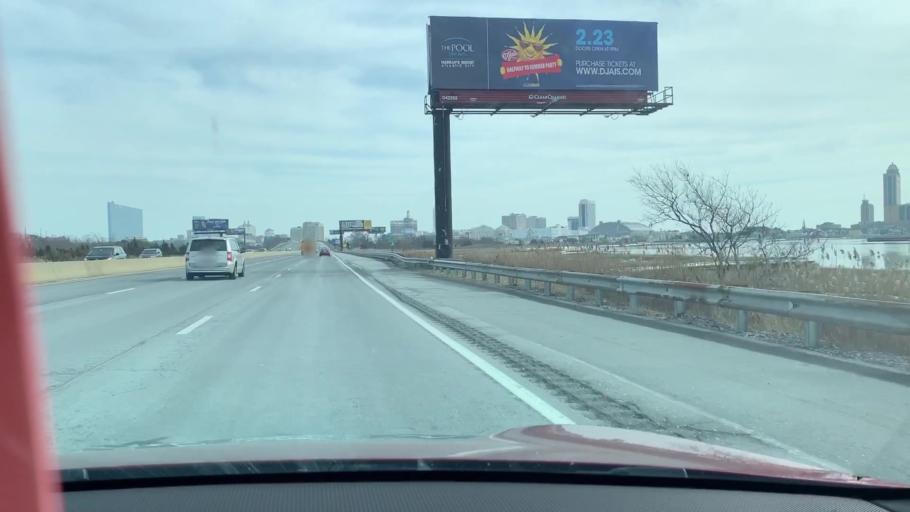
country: US
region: New Jersey
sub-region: Atlantic County
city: Atlantic City
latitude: 39.3664
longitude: -74.4552
